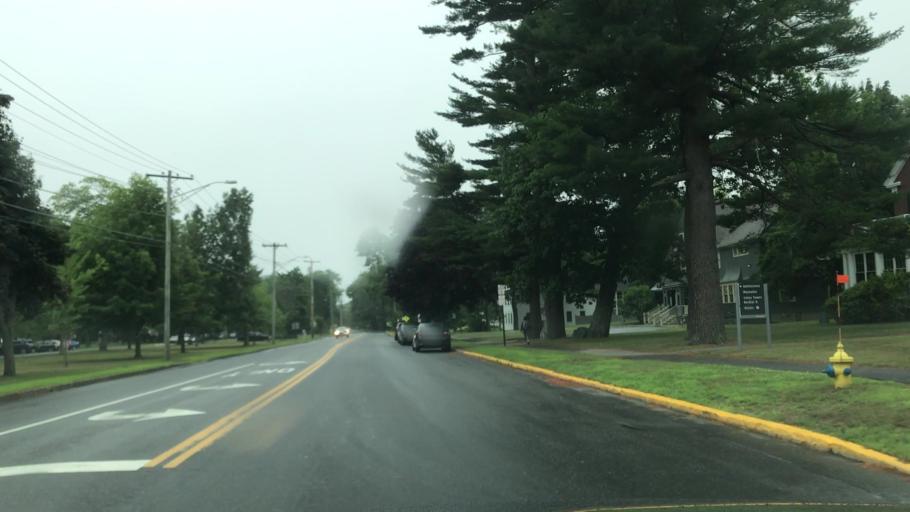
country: US
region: Maine
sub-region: Cumberland County
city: Brunswick
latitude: 43.9083
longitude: -69.9647
